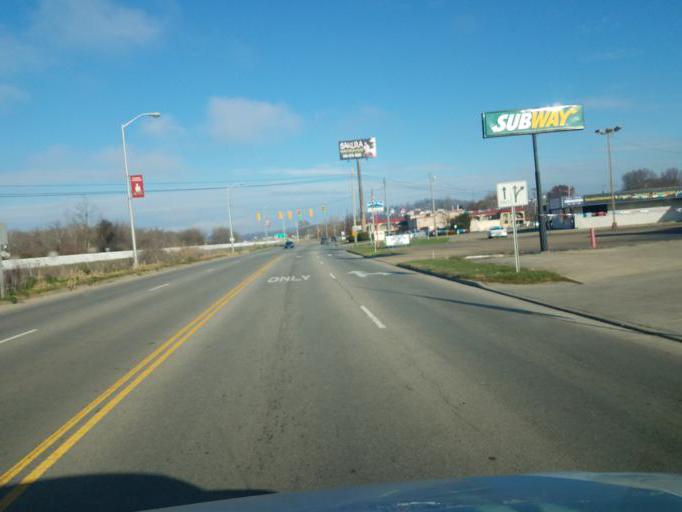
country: US
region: Ohio
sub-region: Scioto County
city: Wheelersburg
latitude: 38.7224
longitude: -82.8593
